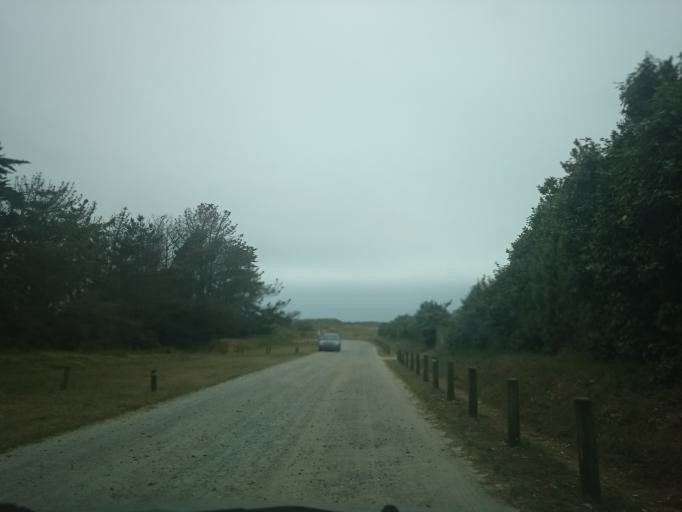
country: FR
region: Brittany
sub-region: Departement du Finistere
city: Saint-Pabu
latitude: 48.5749
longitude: -4.6305
